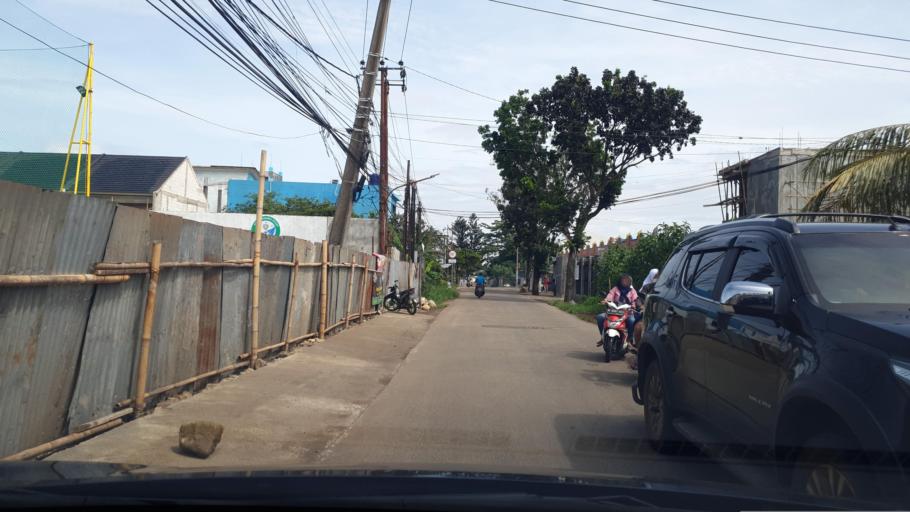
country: ID
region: West Java
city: Sawangan
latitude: -6.4062
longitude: 106.7702
